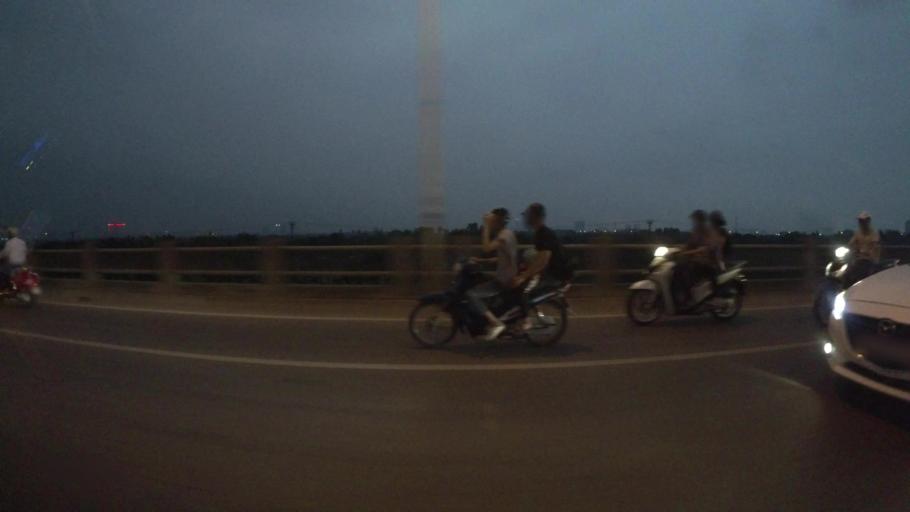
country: VN
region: Ha Noi
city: Hoan Kiem
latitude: 21.0176
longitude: 105.8897
